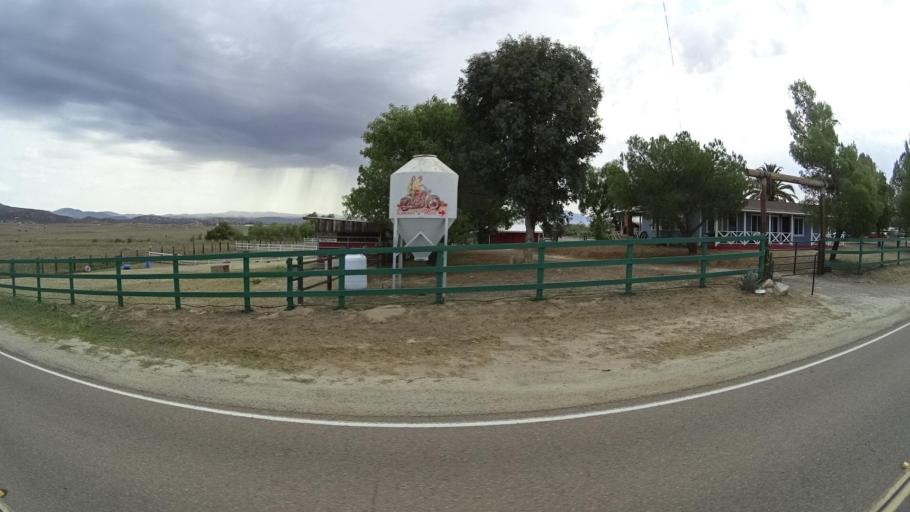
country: US
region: California
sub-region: San Diego County
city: San Pasqual
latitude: 33.0322
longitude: -116.9361
